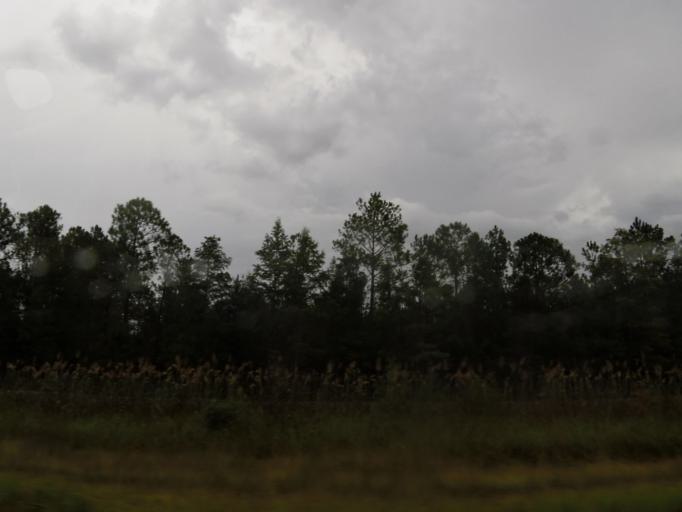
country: US
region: Georgia
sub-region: Wayne County
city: Jesup
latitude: 31.4621
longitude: -81.7110
